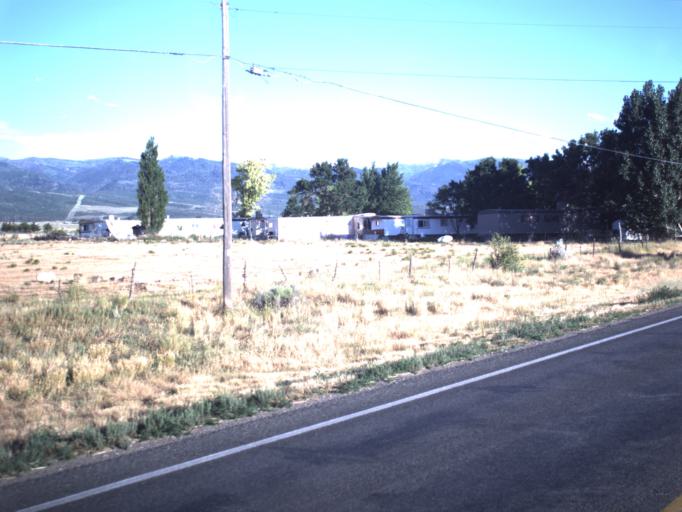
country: US
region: Utah
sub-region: Sanpete County
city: Mount Pleasant
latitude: 39.5660
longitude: -111.4555
